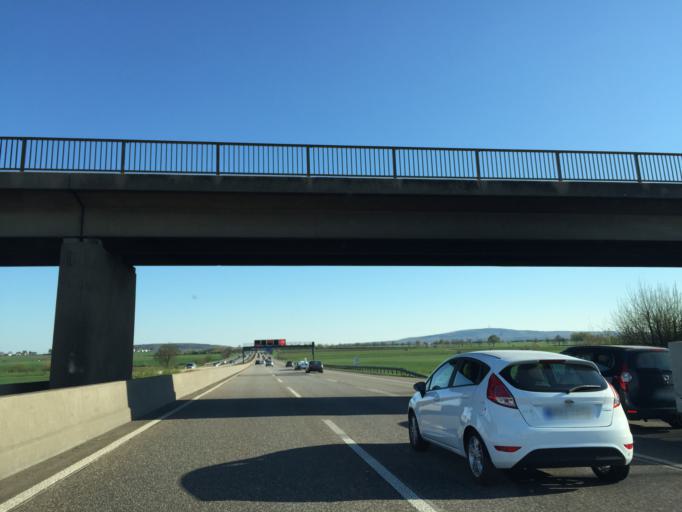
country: DE
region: Hesse
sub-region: Regierungsbezirk Darmstadt
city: Butzbach
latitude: 50.4160
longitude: 8.6989
